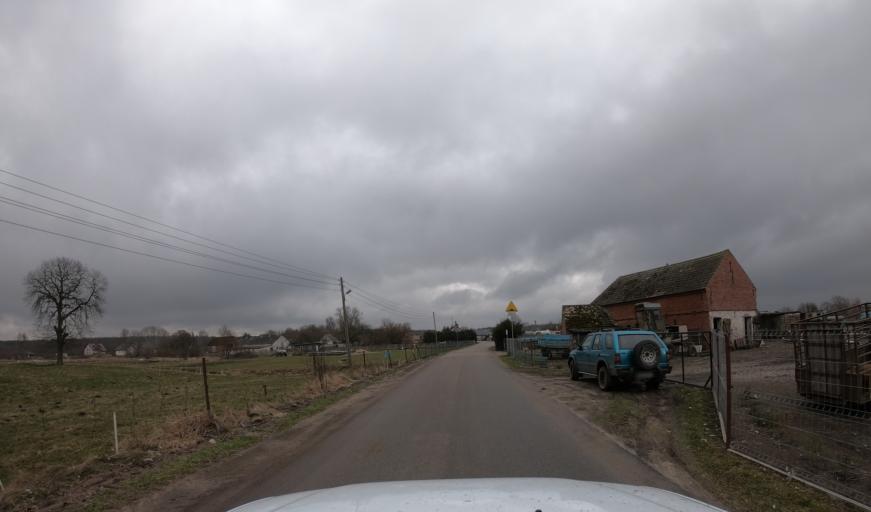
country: PL
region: West Pomeranian Voivodeship
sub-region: Powiat gryficki
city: Pobierowo
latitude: 54.0235
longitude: 14.9602
